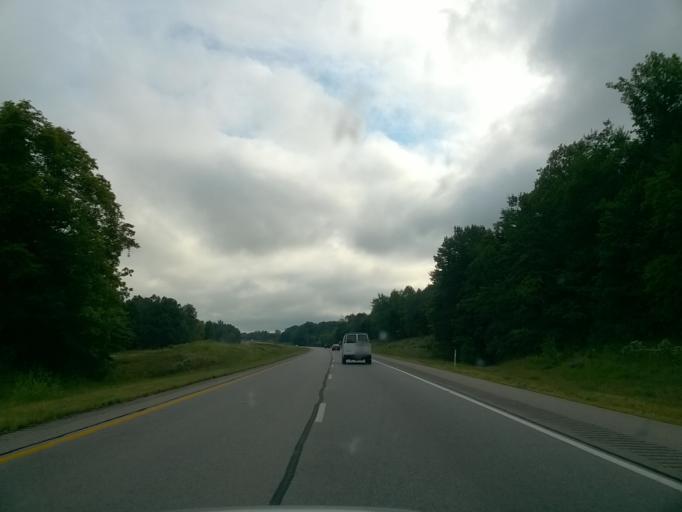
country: US
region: Indiana
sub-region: Floyd County
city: Georgetown
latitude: 38.2570
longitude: -86.0157
